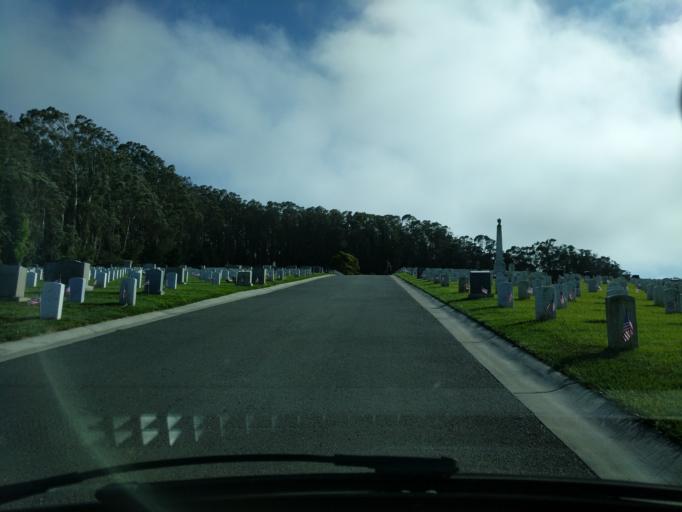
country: US
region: California
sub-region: San Francisco County
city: San Francisco
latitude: 37.7995
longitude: -122.4641
